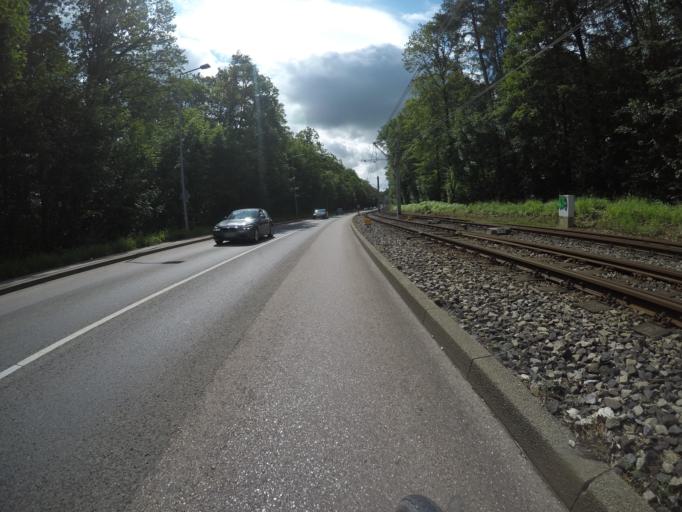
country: DE
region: Baden-Wuerttemberg
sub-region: Regierungsbezirk Stuttgart
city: Stuttgart-Ost
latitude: 48.7529
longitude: 9.1970
